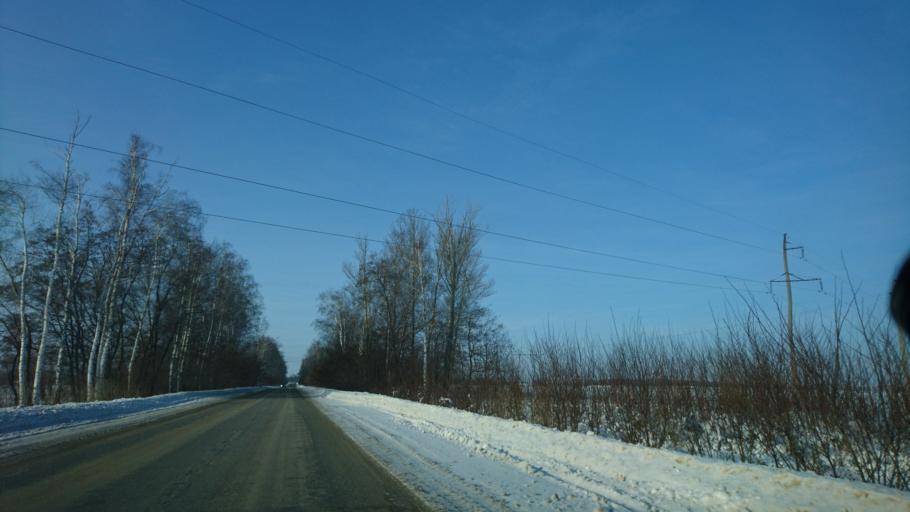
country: RU
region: Belgorod
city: Severnyy
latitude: 50.7289
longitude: 36.5414
